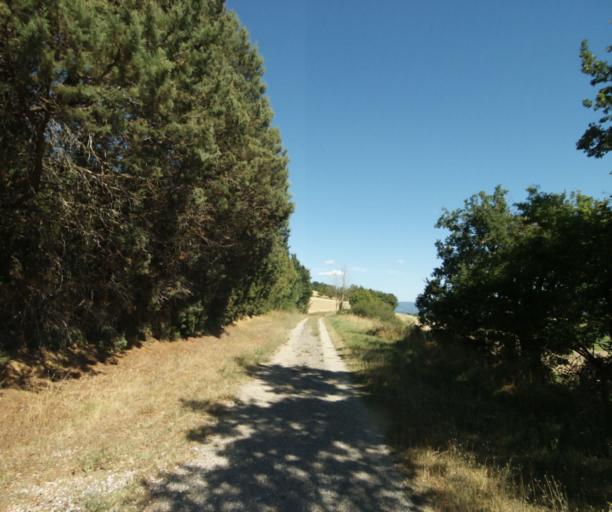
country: FR
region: Midi-Pyrenees
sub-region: Departement de la Haute-Garonne
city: Saint-Felix-Lauragais
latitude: 43.5167
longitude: 1.9174
